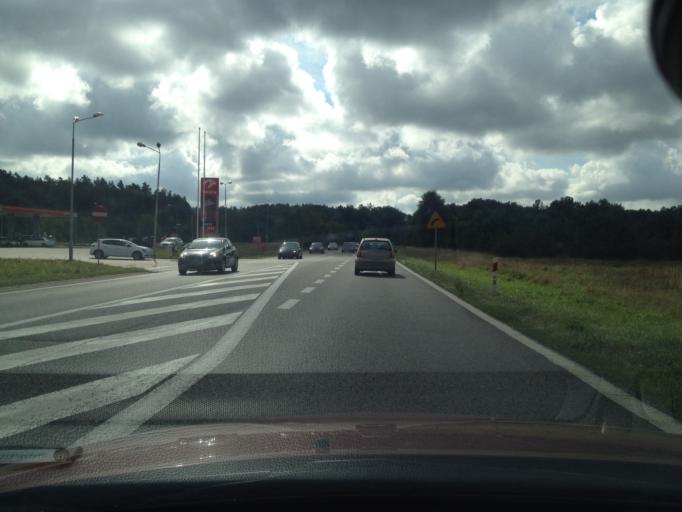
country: PL
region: West Pomeranian Voivodeship
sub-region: Powiat goleniowski
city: Przybiernow
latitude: 53.6791
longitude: 14.8109
